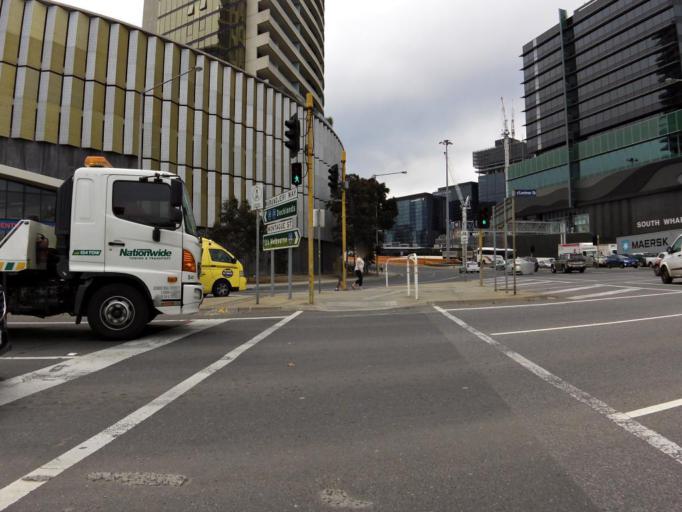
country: AU
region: Victoria
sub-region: Melbourne
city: Docklands
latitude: -37.8253
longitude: 144.9478
